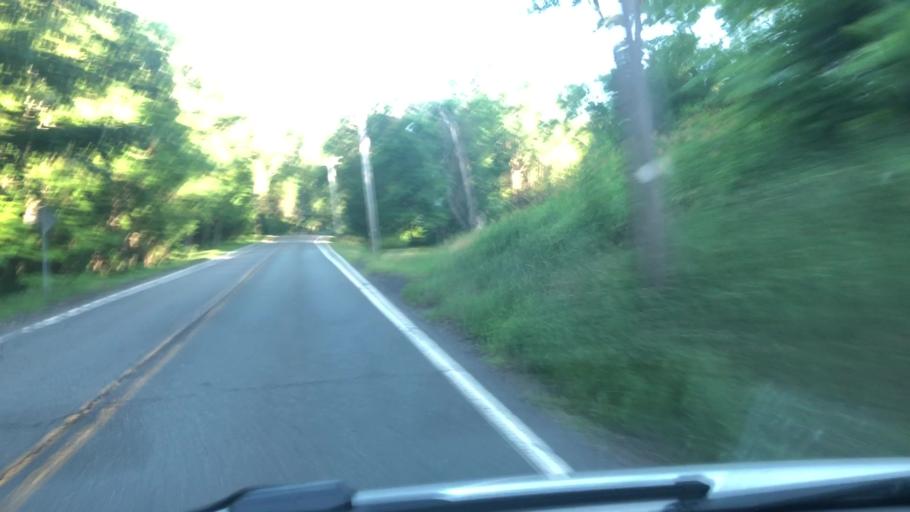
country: US
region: Massachusetts
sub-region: Hampshire County
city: Williamsburg
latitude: 42.4260
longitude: -72.7821
